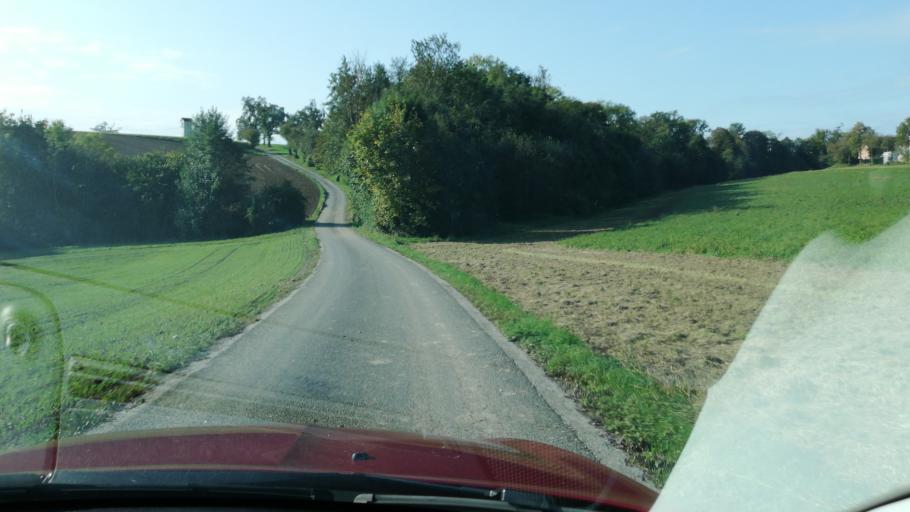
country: AT
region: Upper Austria
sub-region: Politischer Bezirk Kirchdorf an der Krems
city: Kremsmunster
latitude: 48.0978
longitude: 14.1682
